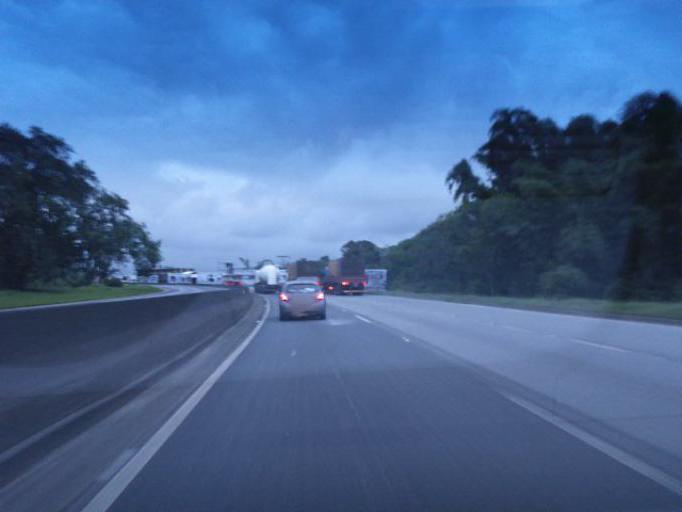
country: BR
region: Santa Catarina
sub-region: Barra Velha
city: Barra Velha
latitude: -26.5560
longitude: -48.7205
